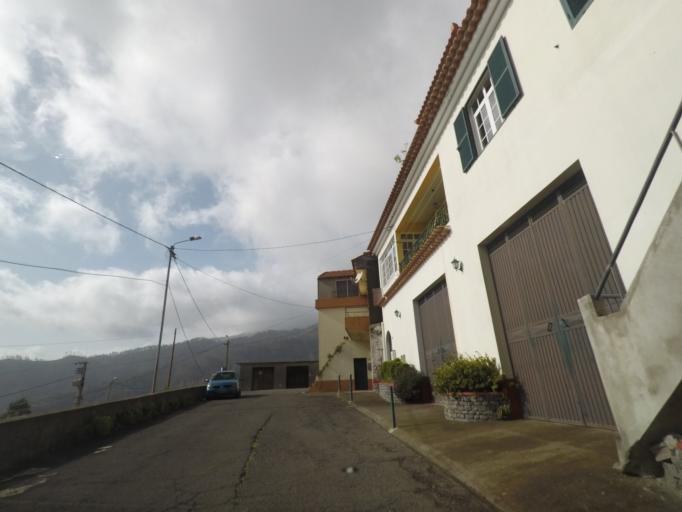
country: PT
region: Madeira
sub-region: Ribeira Brava
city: Campanario
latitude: 32.7057
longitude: -17.0289
